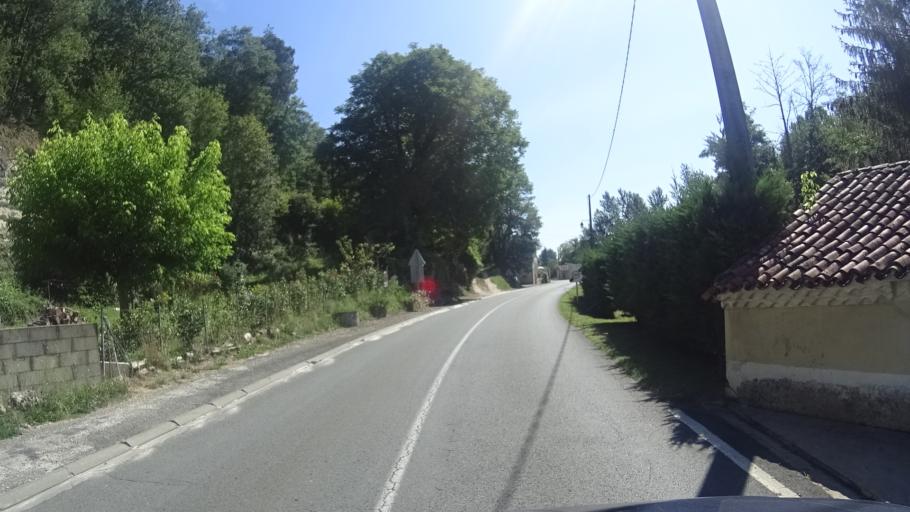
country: FR
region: Aquitaine
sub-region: Departement de la Dordogne
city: Sourzac
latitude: 45.0182
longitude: 0.4025
